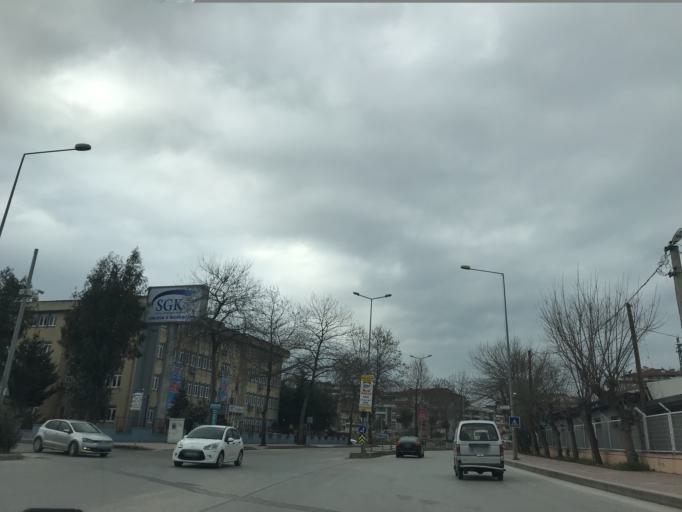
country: TR
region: Yalova
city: Yalova
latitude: 40.6516
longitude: 29.2604
